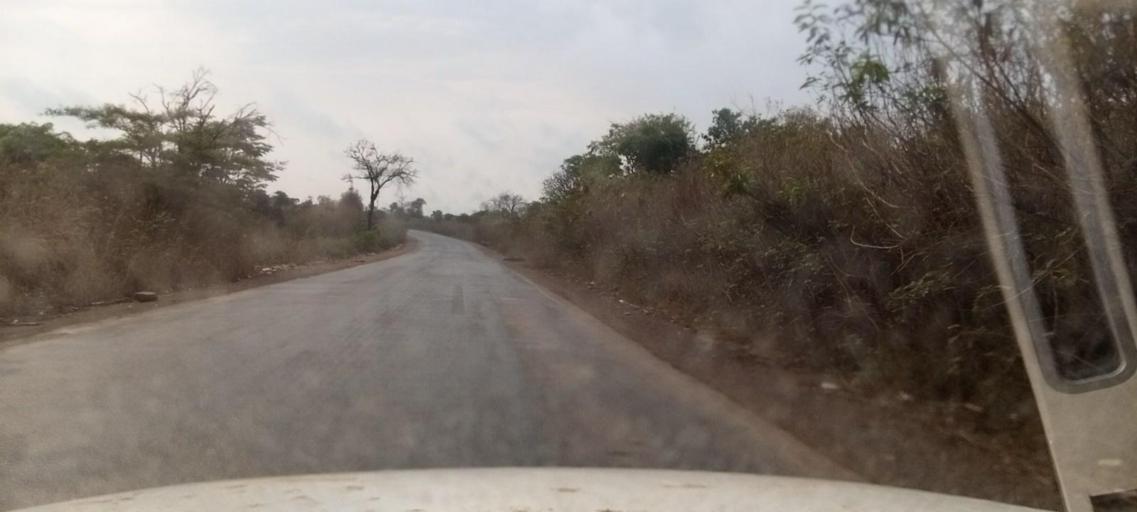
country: CD
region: Katanga
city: Lubumbashi
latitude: -11.2711
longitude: 27.2193
